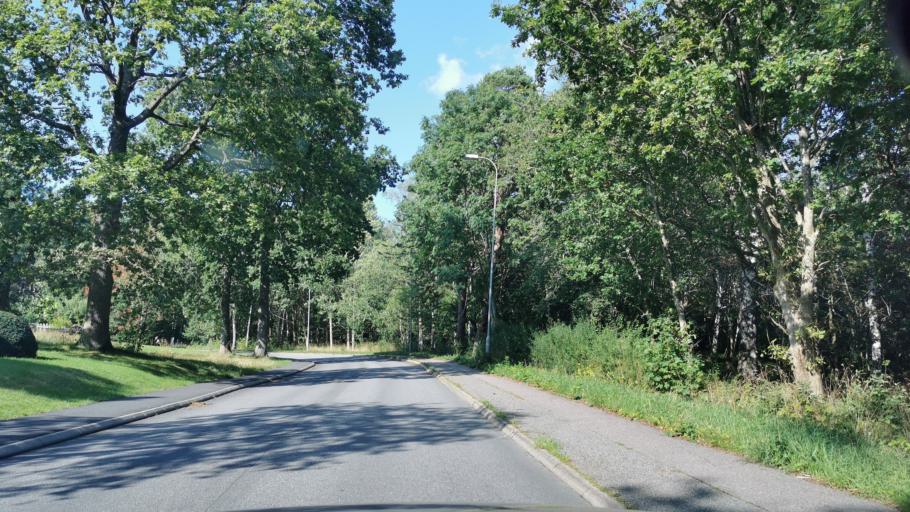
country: SE
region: Vaestra Goetaland
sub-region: Goteborg
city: Majorna
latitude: 57.6436
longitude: 11.9107
